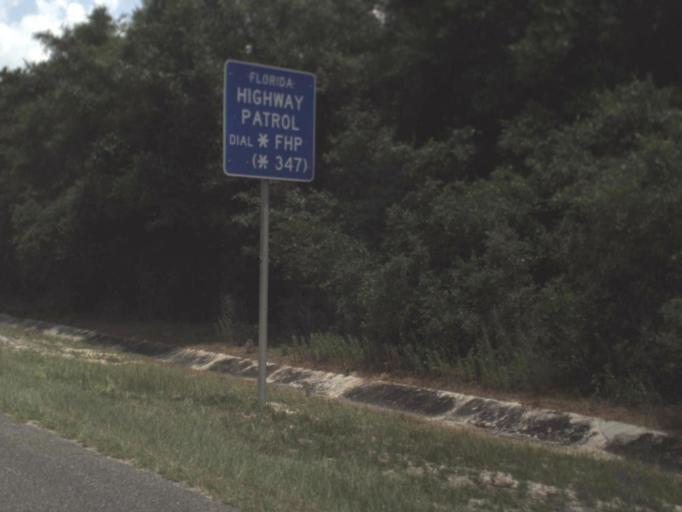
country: US
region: Florida
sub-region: Putnam County
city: Crescent City
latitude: 29.3716
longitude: -81.7357
